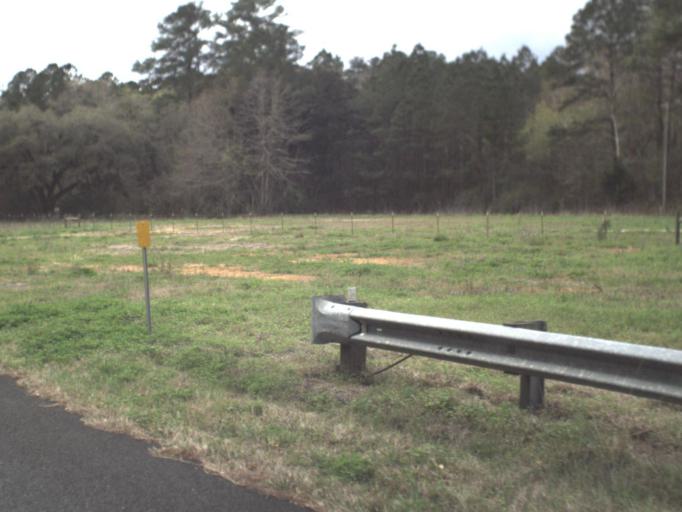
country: US
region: Georgia
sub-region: Grady County
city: Cairo
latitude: 30.6698
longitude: -84.1625
